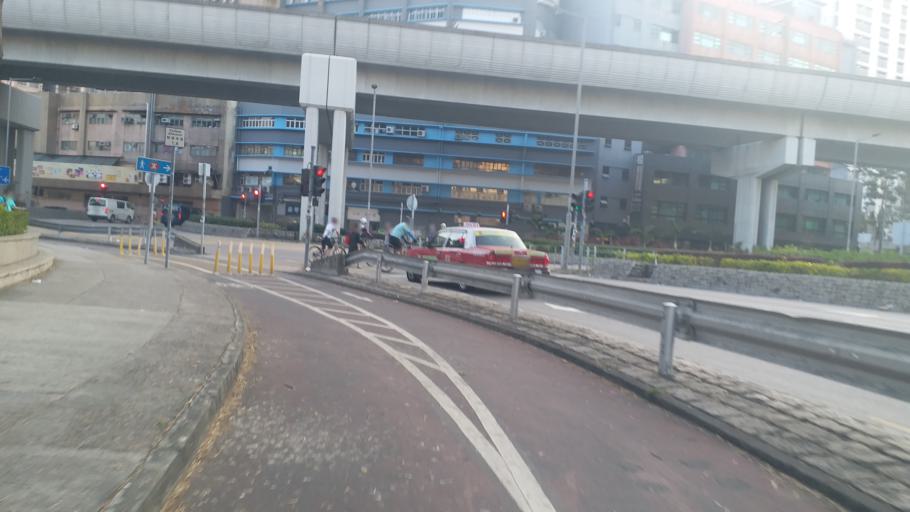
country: HK
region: Yuen Long
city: Yuen Long Kau Hui
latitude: 22.4478
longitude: 114.0296
